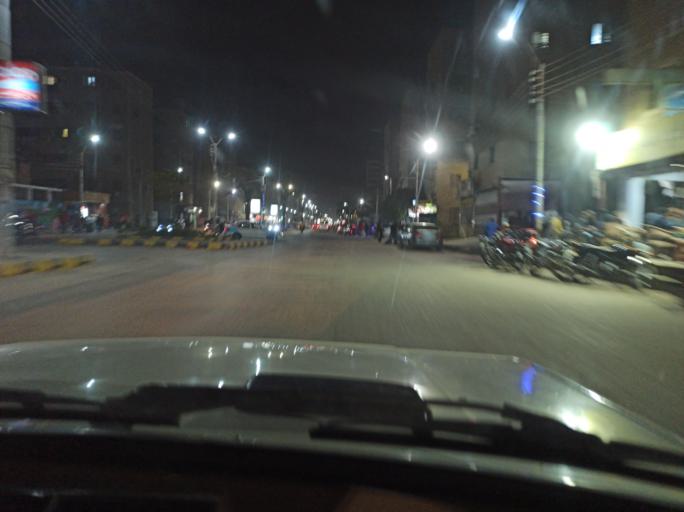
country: EG
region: Muhafazat Bani Suwayf
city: Bani Suwayf
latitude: 29.0717
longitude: 31.1081
